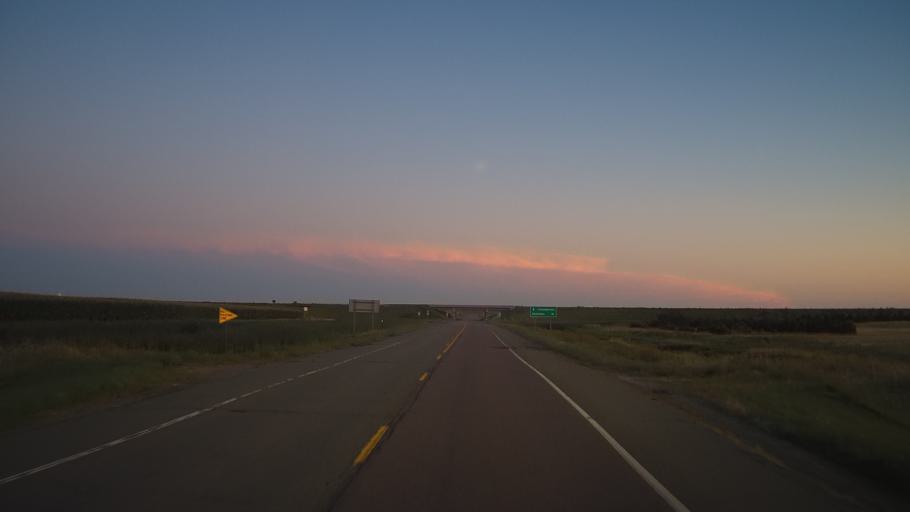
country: US
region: South Dakota
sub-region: Lyman County
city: Kennebec
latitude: 43.8678
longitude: -99.6060
